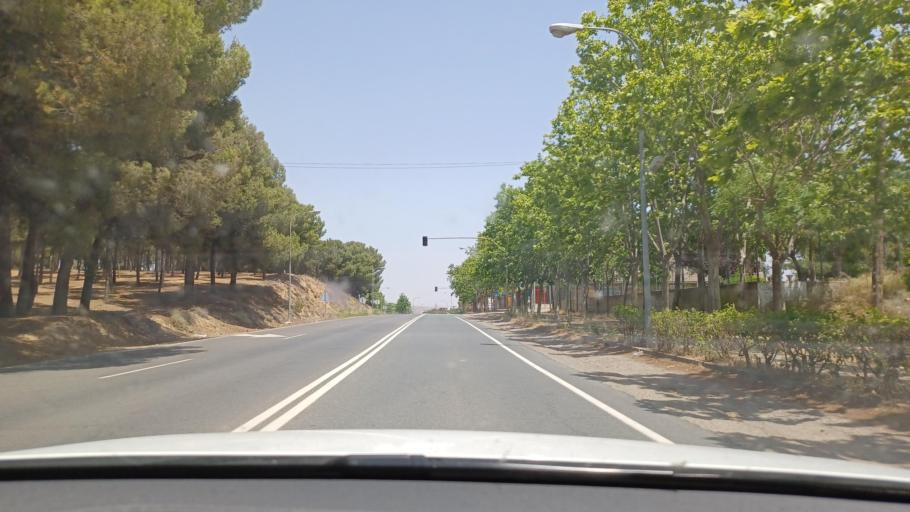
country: ES
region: Navarre
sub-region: Provincia de Navarra
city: Tudela
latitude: 42.0535
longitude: -1.6116
